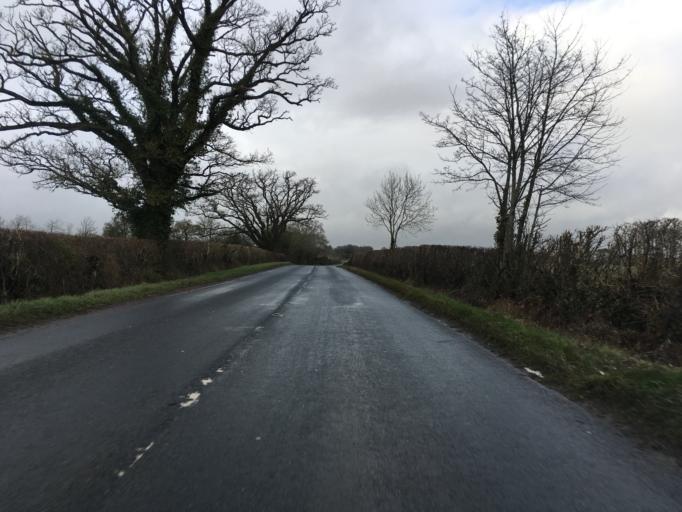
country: GB
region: England
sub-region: Gloucestershire
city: Tetbury
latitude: 51.6175
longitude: -2.1246
